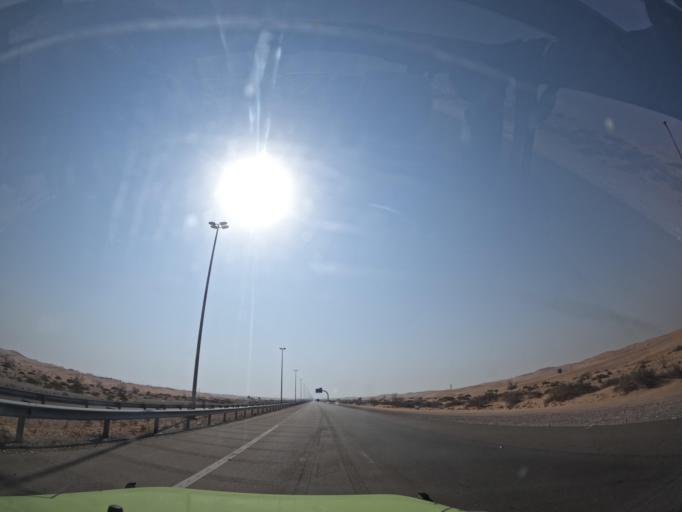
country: OM
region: Al Buraimi
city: Al Buraymi
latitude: 24.5173
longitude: 55.5574
